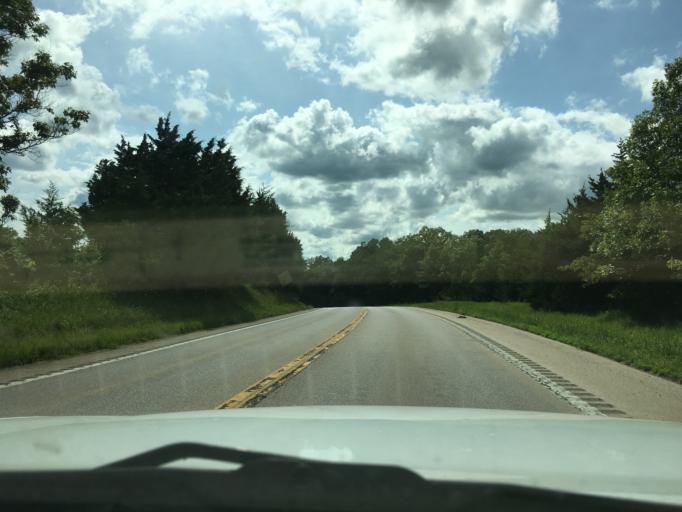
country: US
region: Missouri
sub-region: Franklin County
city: Gerald
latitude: 38.3959
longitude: -91.3511
